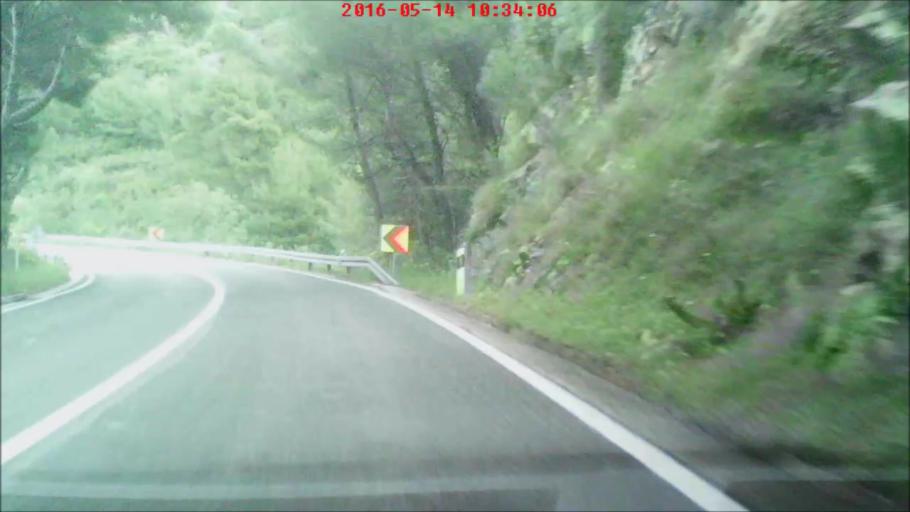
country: HR
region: Dubrovacko-Neretvanska
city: Podgora
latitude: 42.7790
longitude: 17.8888
